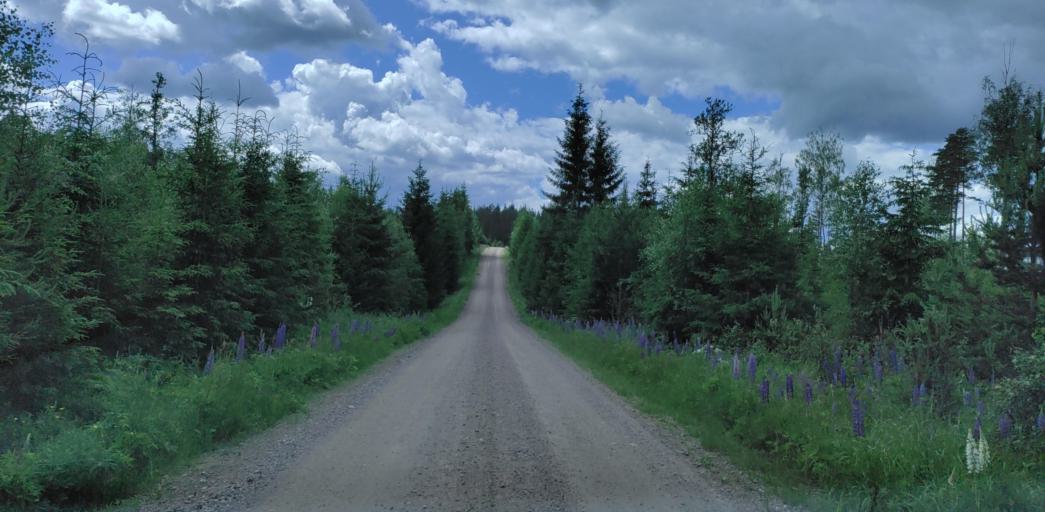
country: SE
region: Vaermland
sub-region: Hagfors Kommun
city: Ekshaerad
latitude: 60.0871
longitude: 13.3267
